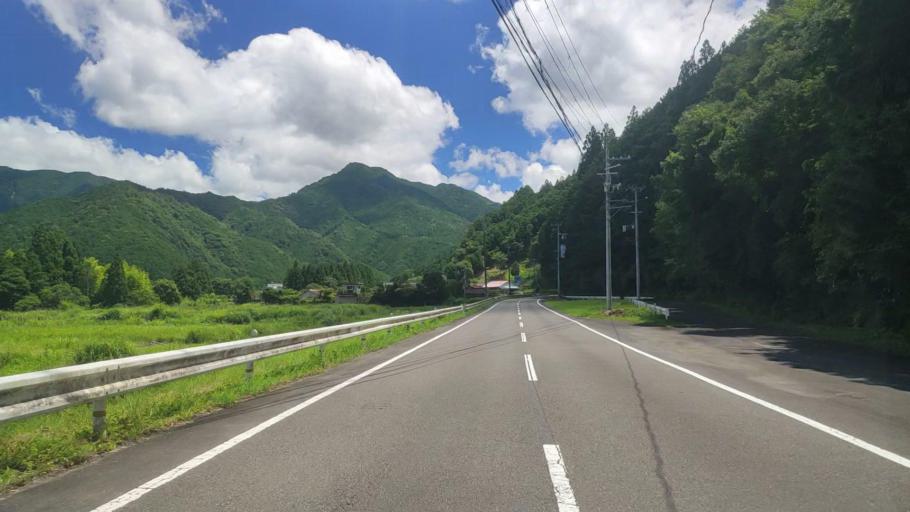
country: JP
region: Mie
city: Owase
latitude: 33.9821
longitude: 136.0362
